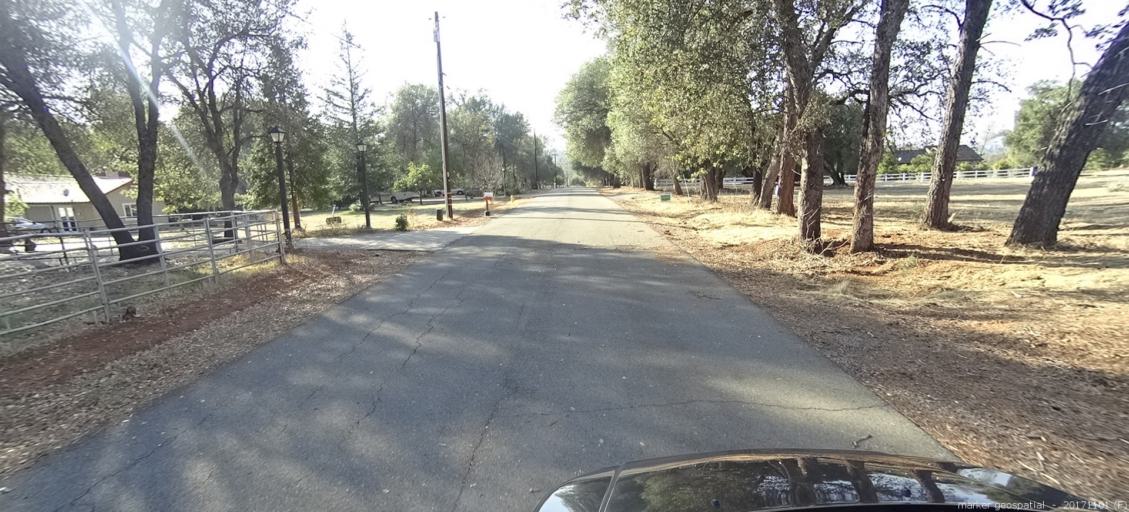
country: US
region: California
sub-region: Shasta County
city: Bella Vista
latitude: 40.6806
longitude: -122.2934
